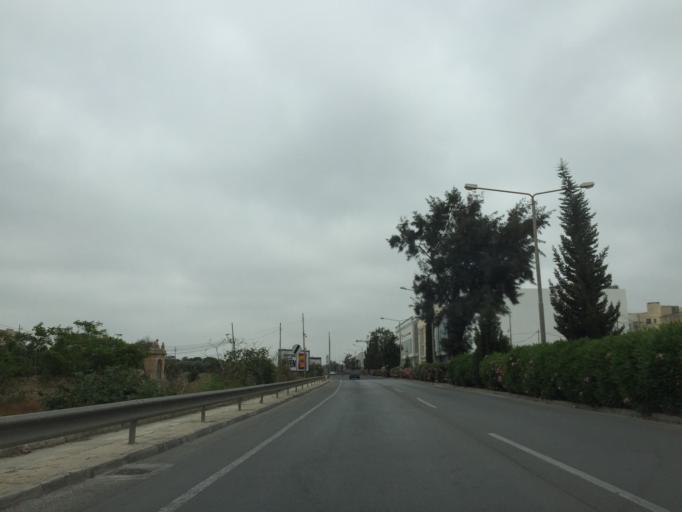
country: MT
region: Saint Venera
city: Santa Venera
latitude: 35.8875
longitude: 14.4656
